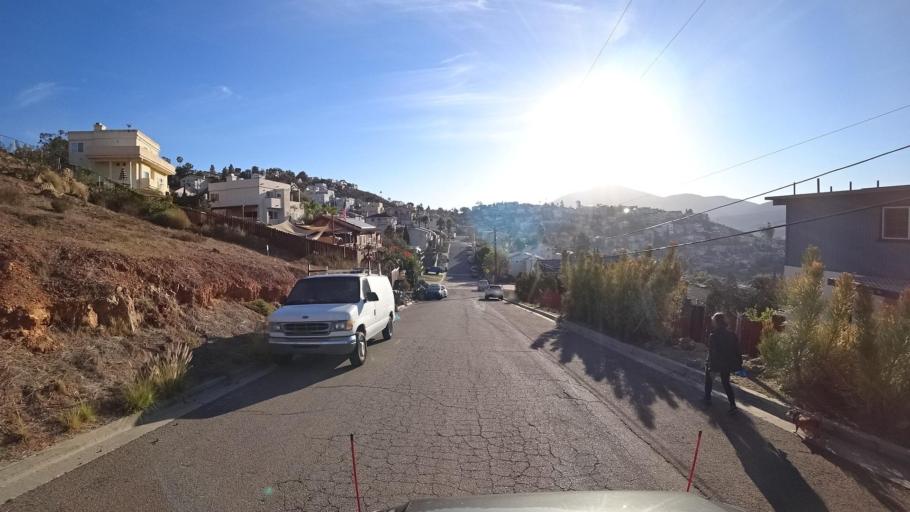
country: US
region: California
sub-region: San Diego County
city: La Presa
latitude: 32.7185
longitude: -116.9930
